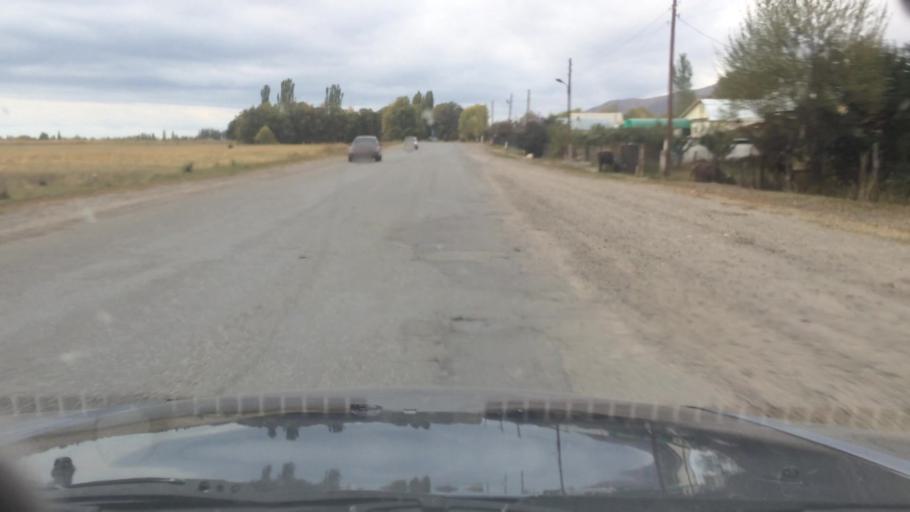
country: KG
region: Ysyk-Koel
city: Tyup
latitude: 42.7785
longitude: 78.2110
